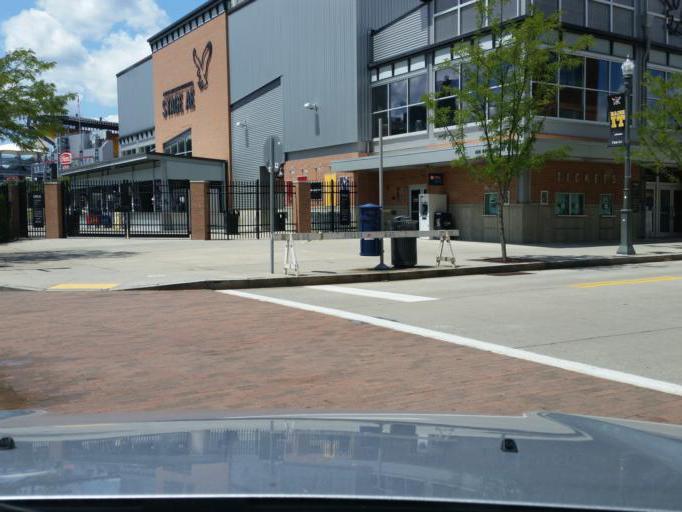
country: US
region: Pennsylvania
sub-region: Allegheny County
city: Pittsburgh
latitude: 40.4459
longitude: -80.0115
